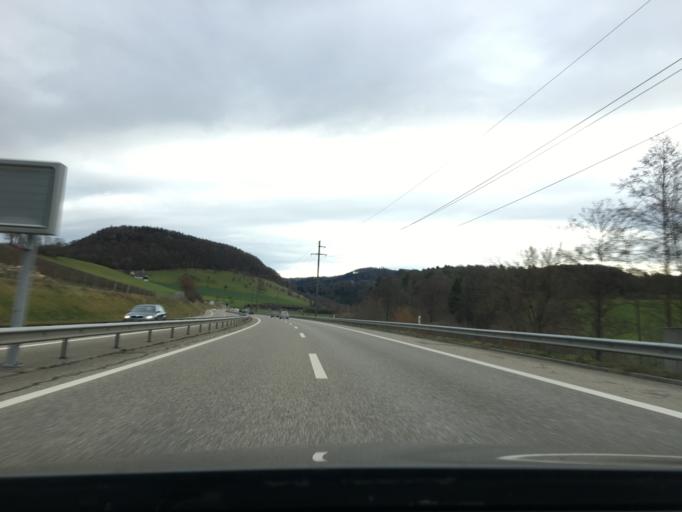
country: CH
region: Aargau
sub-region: Bezirk Laufenburg
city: Sulz
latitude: 47.4883
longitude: 8.0870
